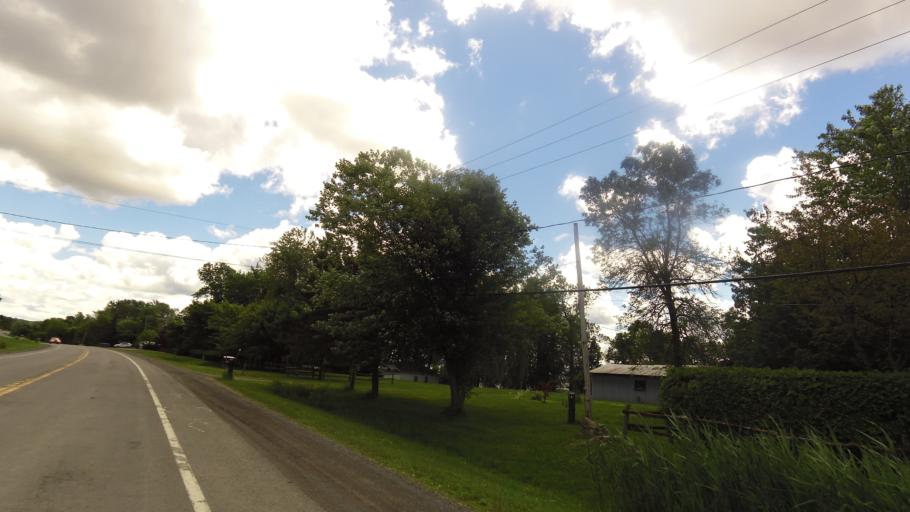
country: CA
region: Quebec
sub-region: Monteregie
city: Rigaud
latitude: 45.5310
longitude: -74.2387
